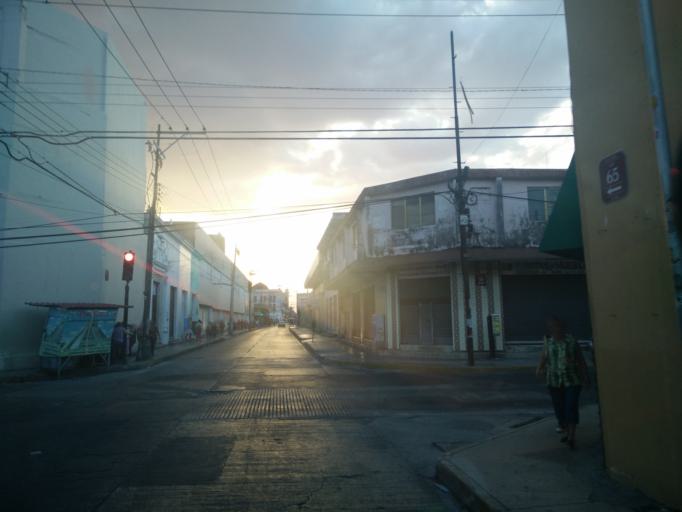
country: MX
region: Yucatan
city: Merida
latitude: 20.9639
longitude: -89.6171
